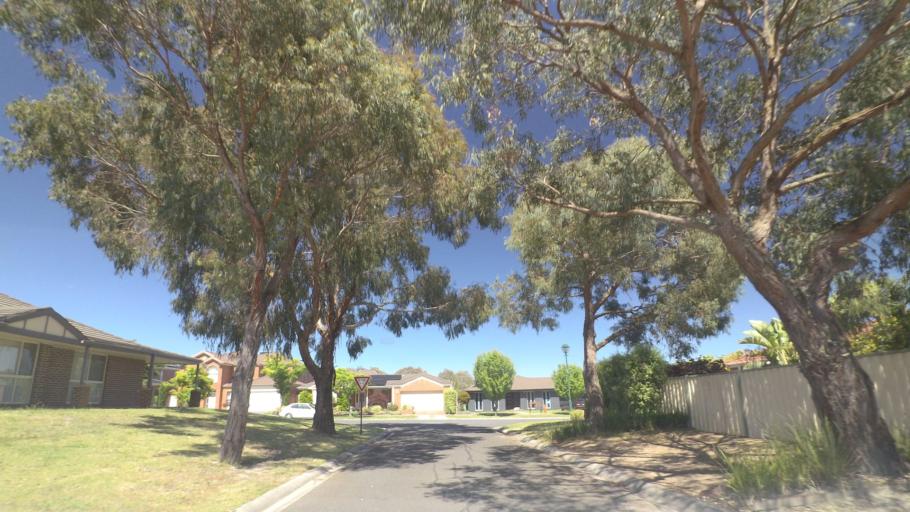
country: AU
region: Victoria
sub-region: Maroondah
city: Croydon Hills
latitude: -37.7884
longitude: 145.2606
